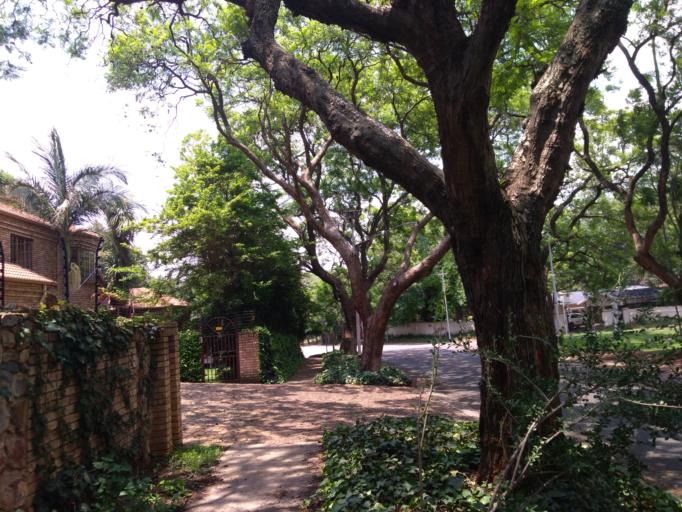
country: ZA
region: Gauteng
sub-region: City of Tshwane Metropolitan Municipality
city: Pretoria
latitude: -25.7621
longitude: 28.2297
